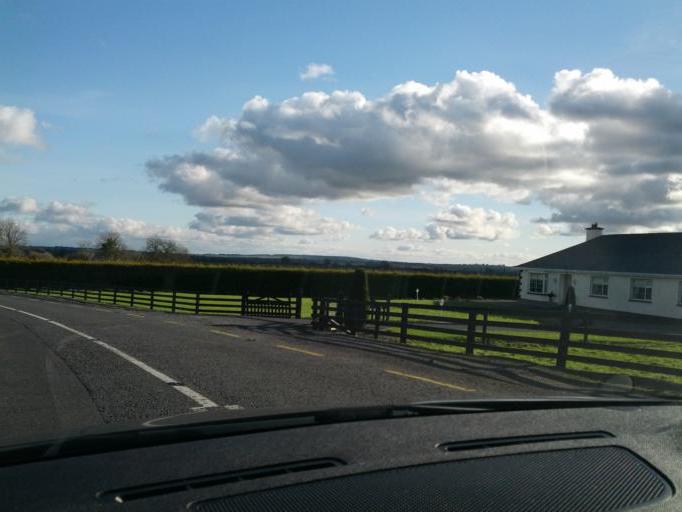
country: IE
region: Connaught
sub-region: Roscommon
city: Roscommon
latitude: 53.6751
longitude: -8.3419
